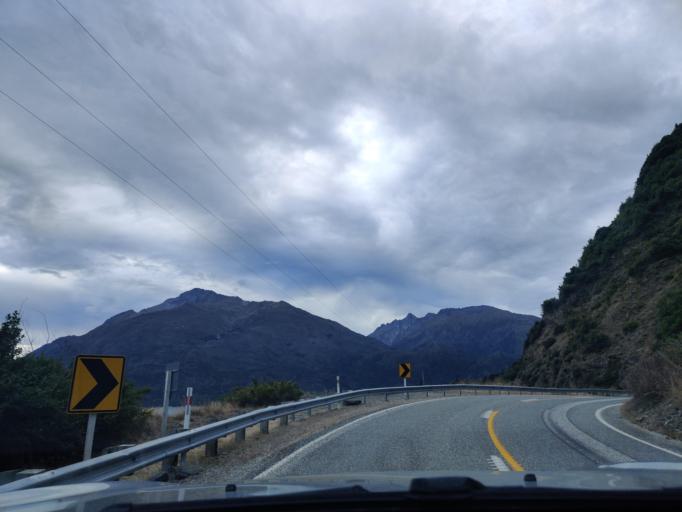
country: NZ
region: Otago
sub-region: Queenstown-Lakes District
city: Wanaka
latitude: -44.3603
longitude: 169.1780
